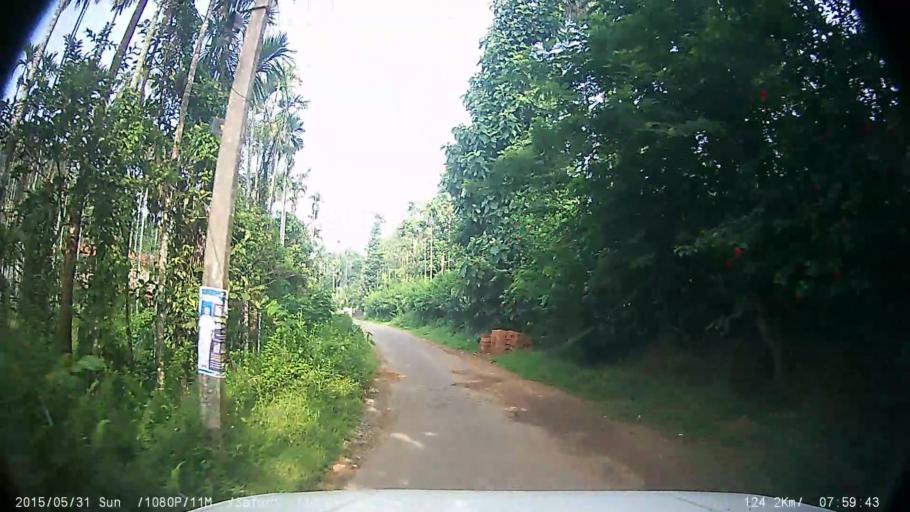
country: IN
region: Kerala
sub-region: Wayanad
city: Kalpetta
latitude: 11.6337
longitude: 76.0553
